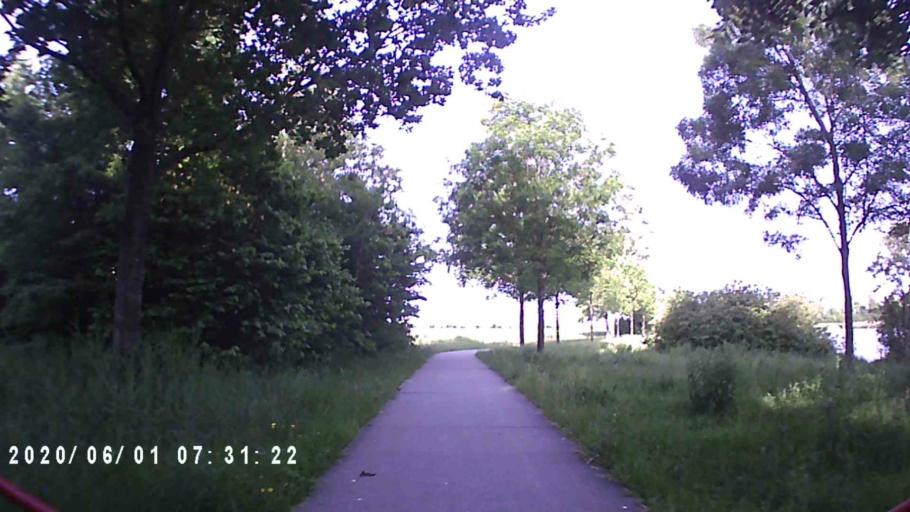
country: NL
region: Friesland
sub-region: Gemeente Dongeradeel
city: Dokkum
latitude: 53.3116
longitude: 6.0022
